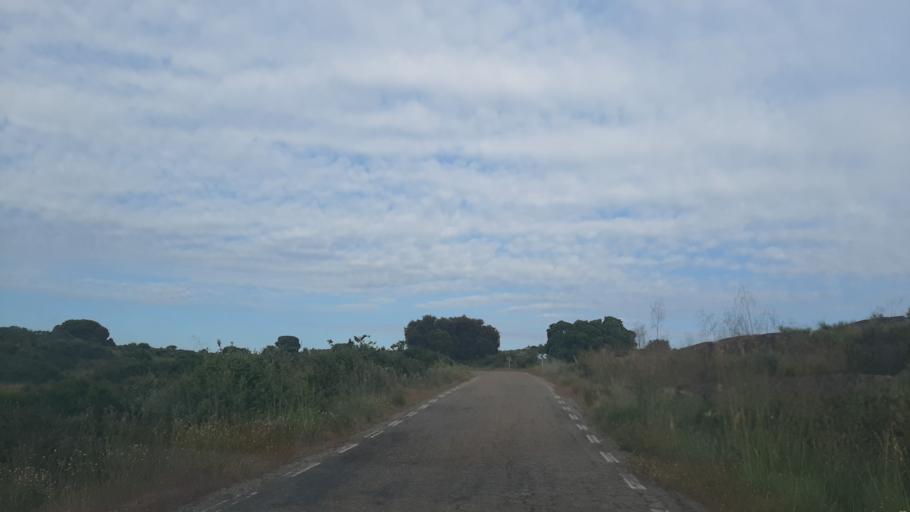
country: ES
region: Castille and Leon
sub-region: Provincia de Salamanca
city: Fuentes de Onoro
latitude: 40.6432
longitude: -6.7887
